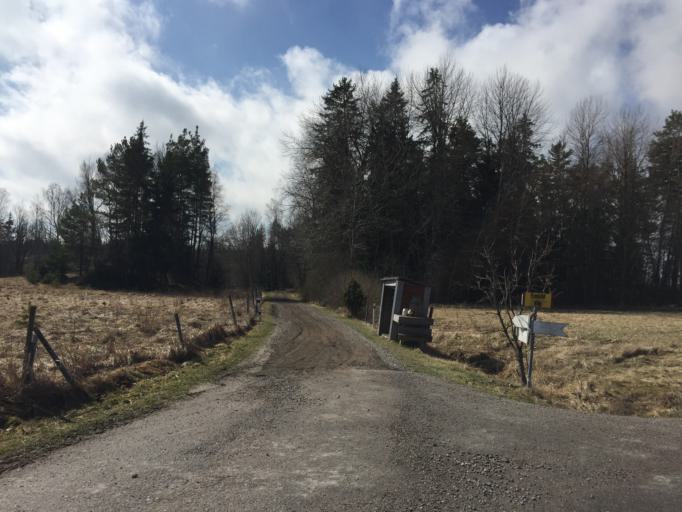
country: SE
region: Soedermanland
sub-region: Gnesta Kommun
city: Gnesta
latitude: 59.0338
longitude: 17.2199
